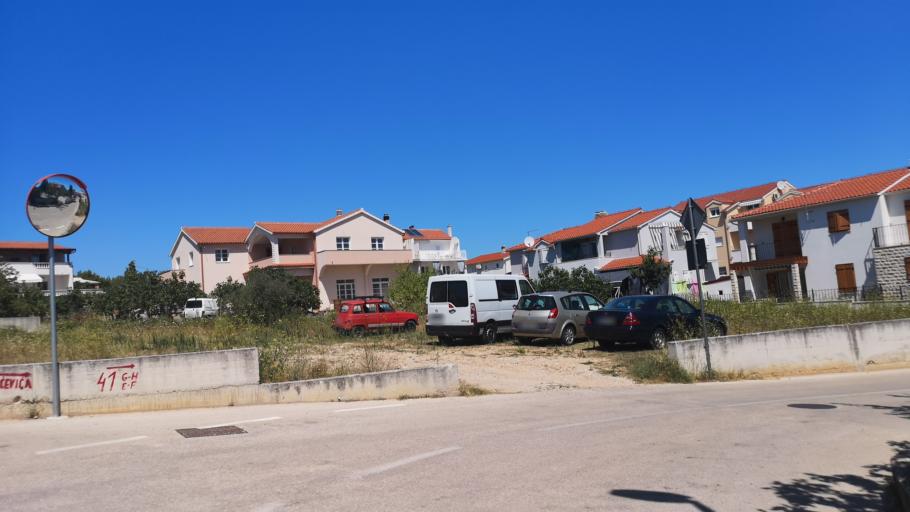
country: HR
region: Sibensko-Kniniska
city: Vodice
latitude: 43.7618
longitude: 15.7685
